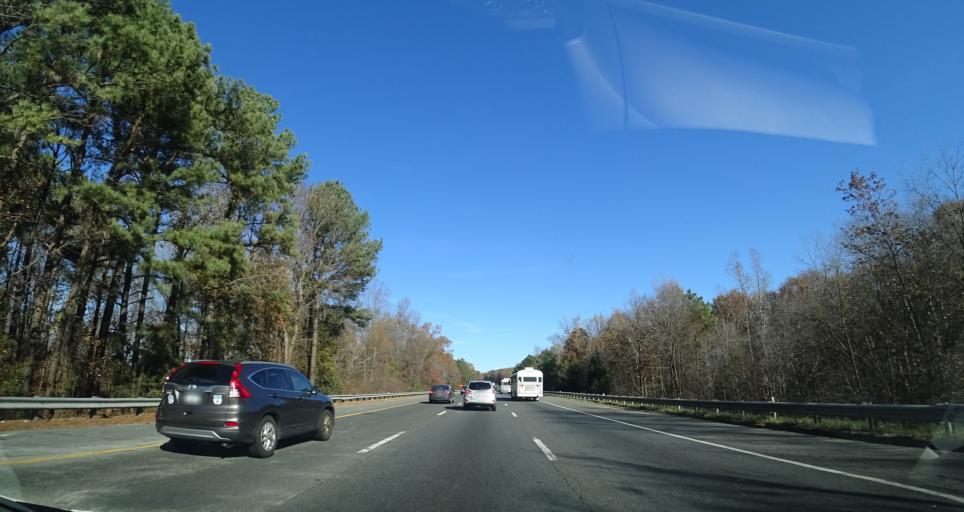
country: US
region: Virginia
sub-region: Spotsylvania County
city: Spotsylvania Courthouse
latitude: 38.1663
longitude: -77.5054
